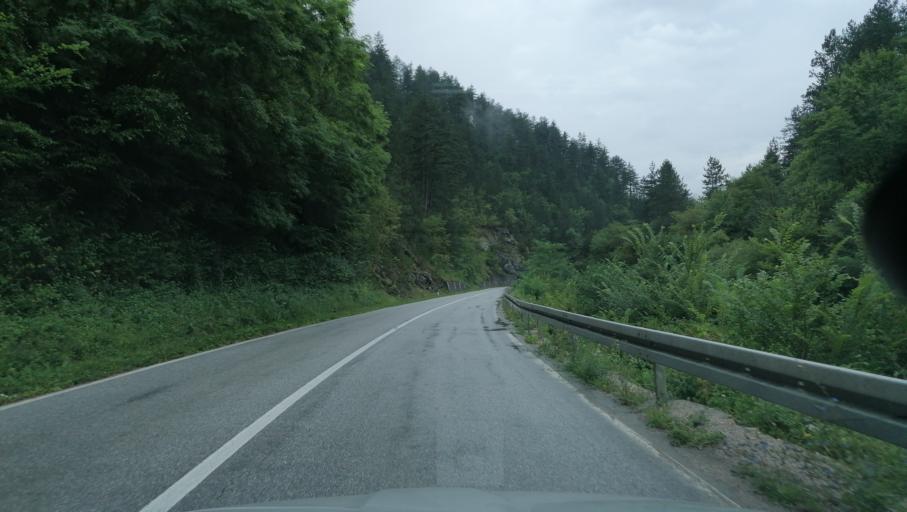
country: RS
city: Durici
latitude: 43.7751
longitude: 19.3790
